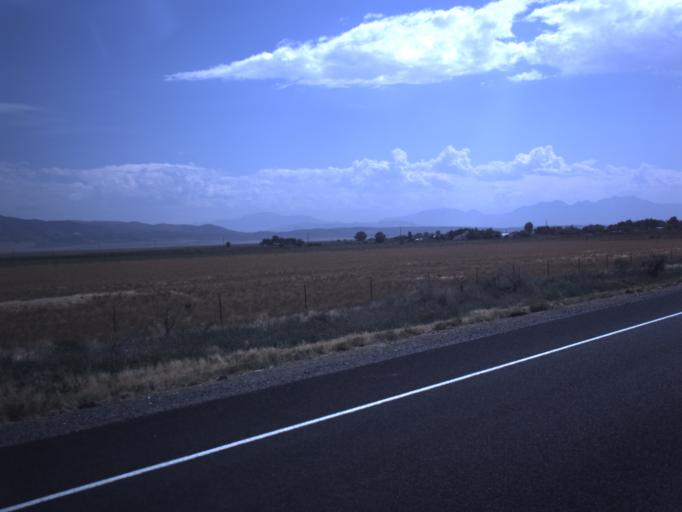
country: US
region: Utah
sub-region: Utah County
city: Eagle Mountain
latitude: 40.2726
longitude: -112.0938
